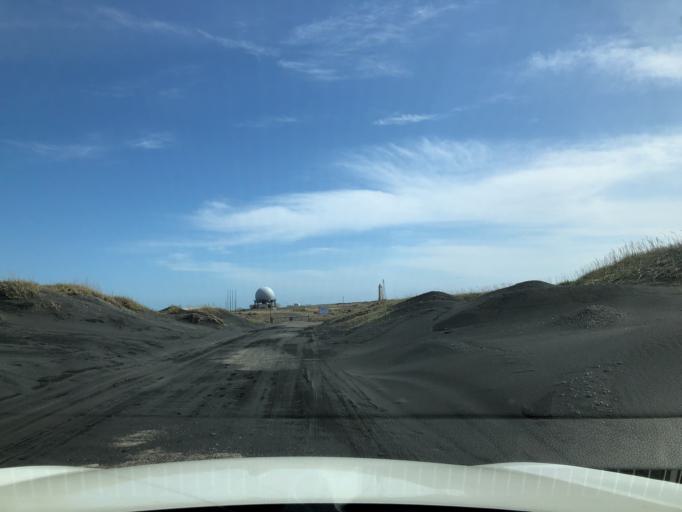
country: IS
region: East
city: Hoefn
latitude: 64.2447
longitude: -14.9725
